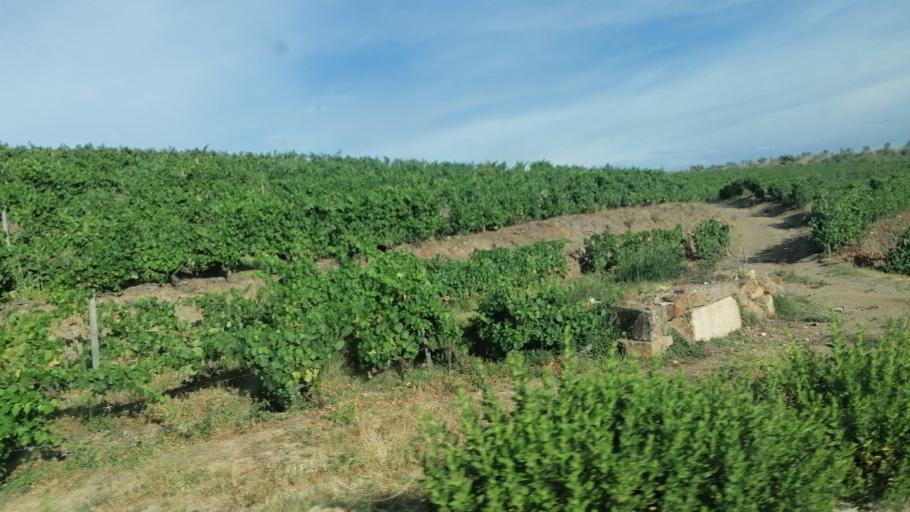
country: PT
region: Viseu
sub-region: Sao Joao da Pesqueira
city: Sao Joao da Pesqueira
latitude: 41.1370
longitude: -7.4375
